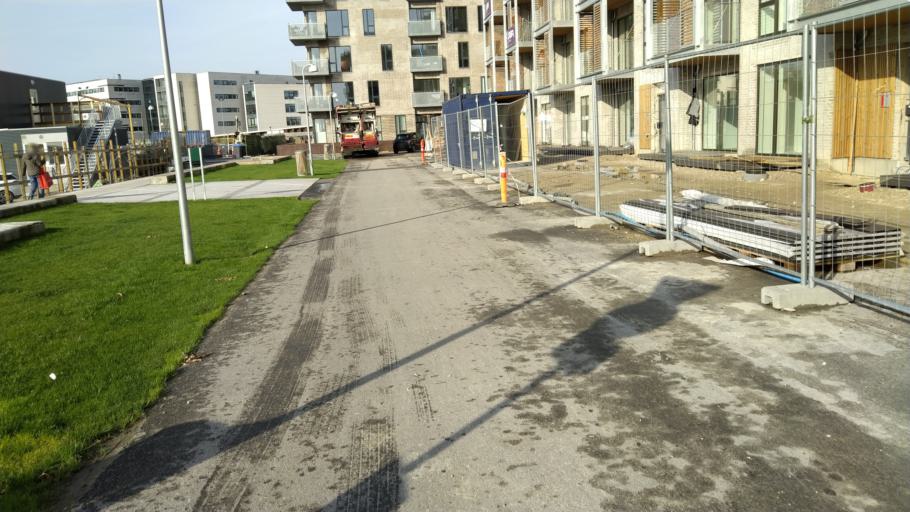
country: DK
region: Capital Region
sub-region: Kobenhavn
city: Christianshavn
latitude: 55.7100
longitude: 12.5965
